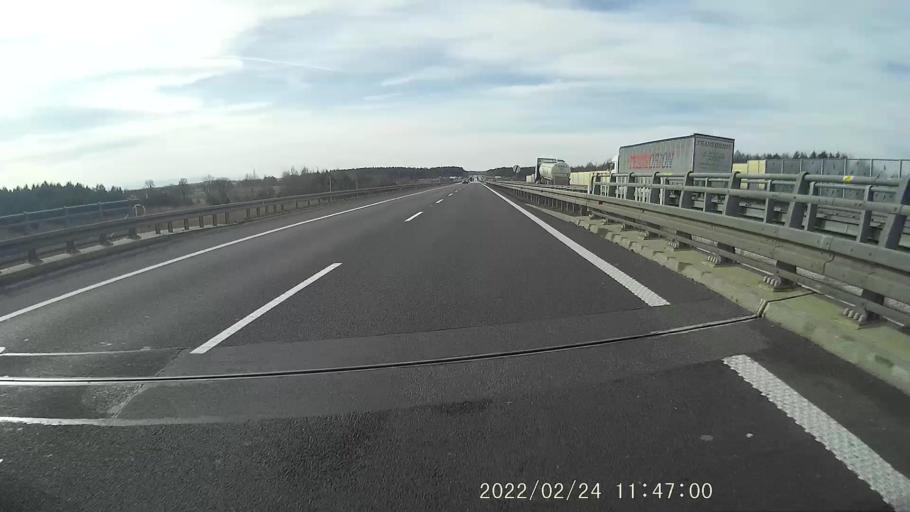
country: PL
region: Lower Silesian Voivodeship
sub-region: Powiat polkowicki
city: Radwanice
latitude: 51.5730
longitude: 15.9483
